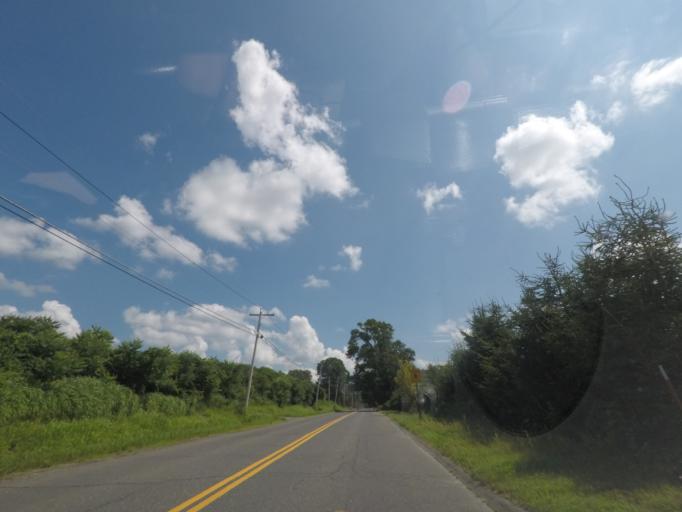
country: US
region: Massachusetts
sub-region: Hampden County
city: Monson
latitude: 42.1258
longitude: -72.3334
